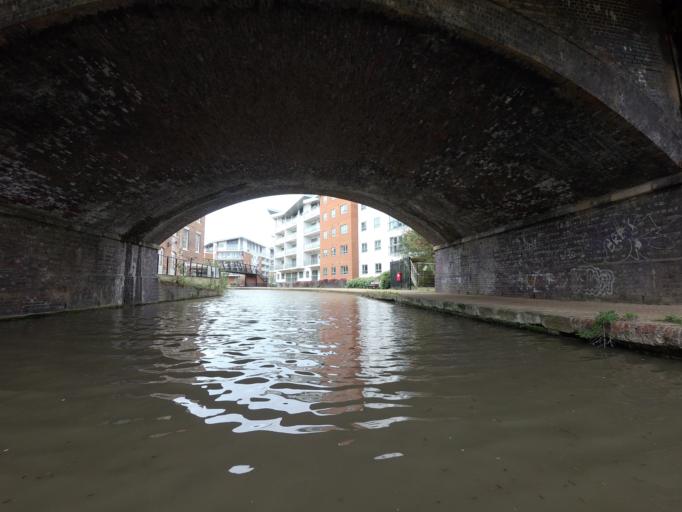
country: GB
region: England
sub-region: Milton Keynes
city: Bradwell
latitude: 52.0644
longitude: -0.8043
